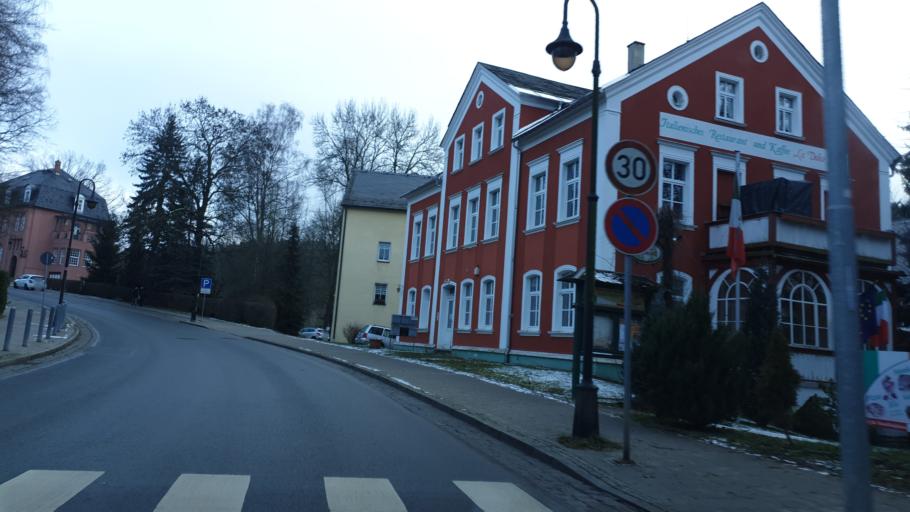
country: DE
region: Saxony
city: Bad Elster
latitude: 50.2787
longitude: 12.2380
